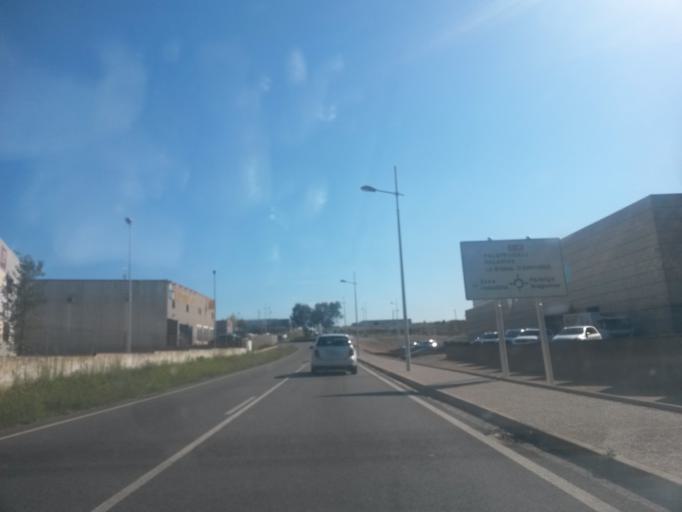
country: ES
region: Catalonia
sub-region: Provincia de Girona
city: Palafrugell
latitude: 41.9292
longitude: 3.1572
